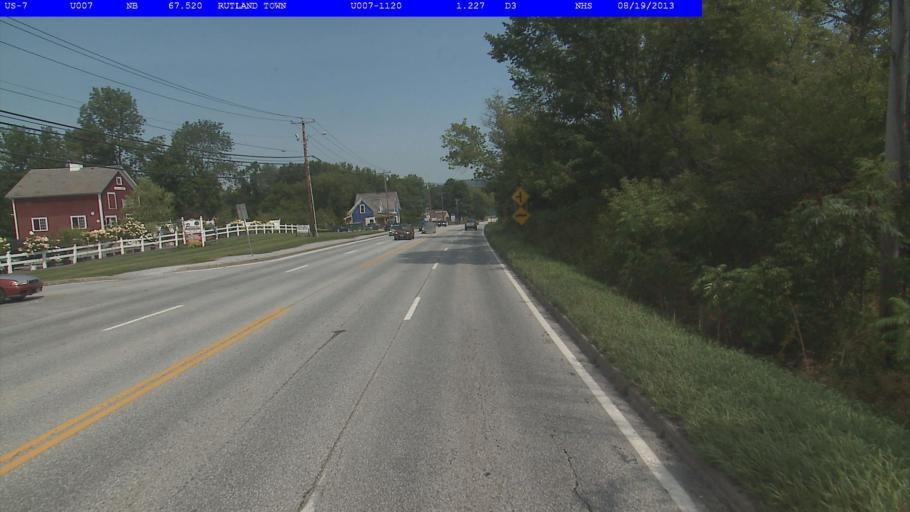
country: US
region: Vermont
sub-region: Rutland County
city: Rutland
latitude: 43.6308
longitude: -72.9762
